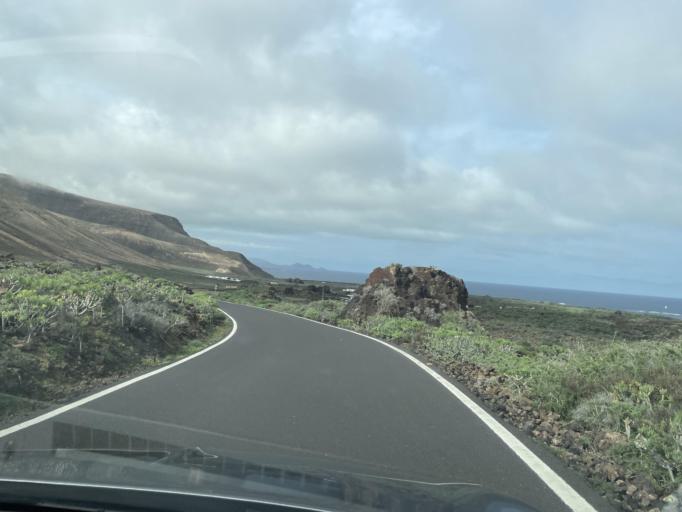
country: ES
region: Canary Islands
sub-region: Provincia de Las Palmas
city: Haria
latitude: 29.1989
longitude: -13.4514
